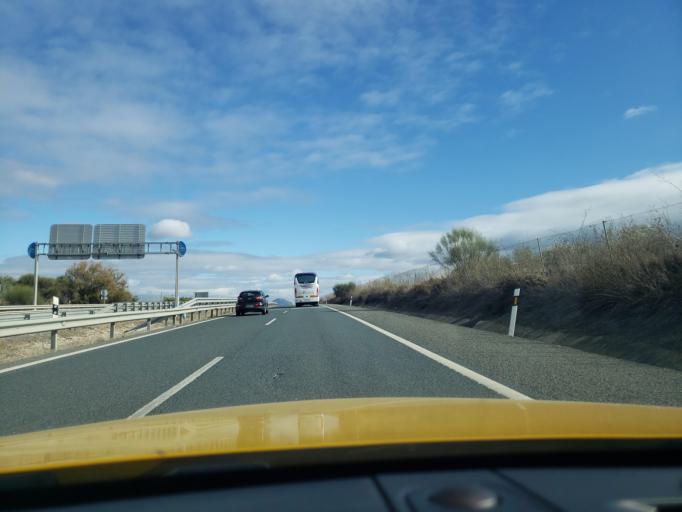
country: ES
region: Andalusia
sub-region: Provincia de Malaga
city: Villanueva de Tapia
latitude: 37.1401
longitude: -4.2736
